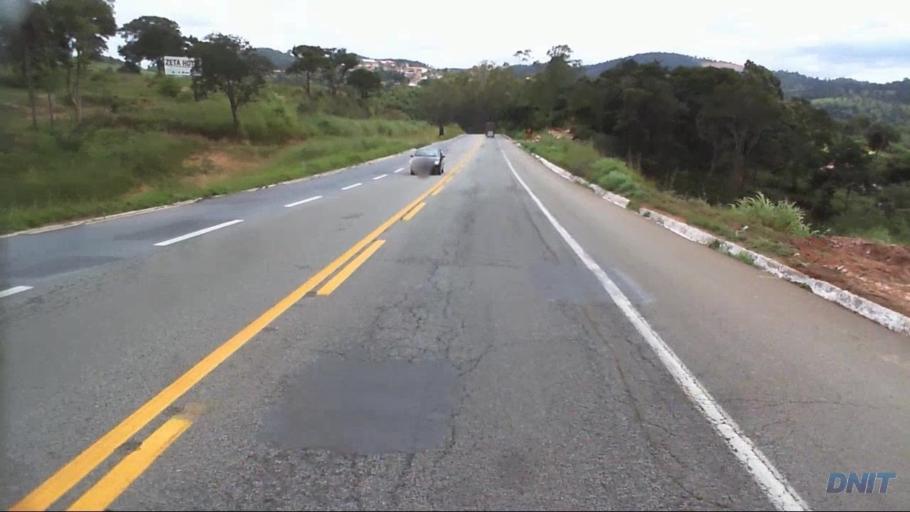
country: BR
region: Minas Gerais
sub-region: Caete
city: Caete
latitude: -19.7255
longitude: -43.5688
